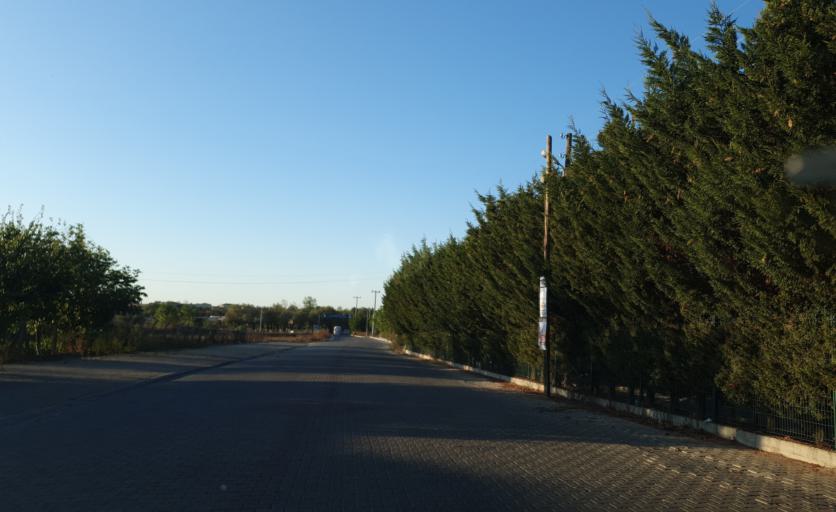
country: TR
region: Tekirdag
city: Beyazkoy
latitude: 41.3071
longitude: 27.7878
